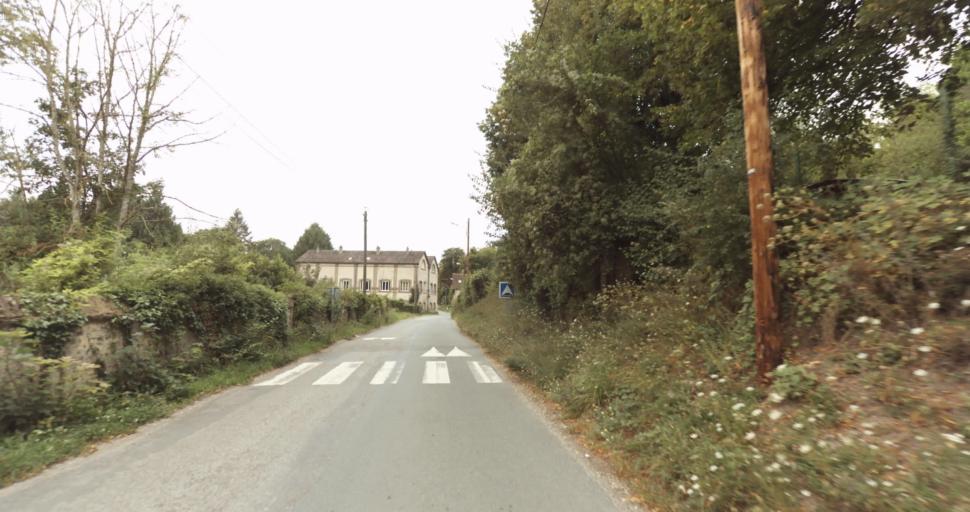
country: FR
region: Centre
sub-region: Departement d'Eure-et-Loir
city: Vert-en-Drouais
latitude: 48.7678
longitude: 1.3016
